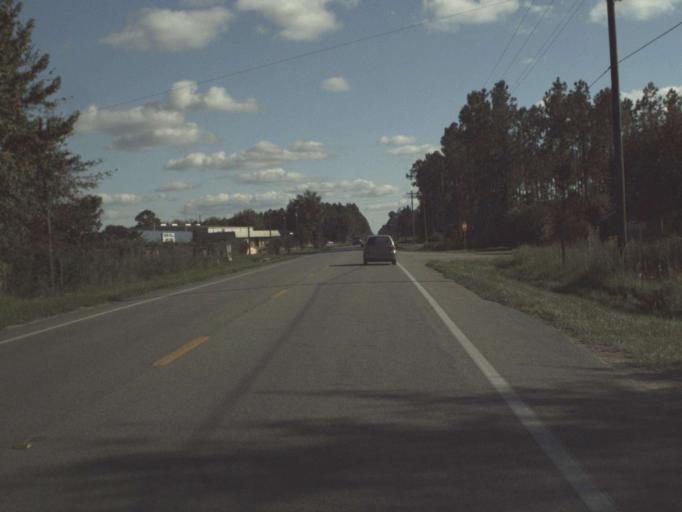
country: US
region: Florida
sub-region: Gulf County
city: Wewahitchka
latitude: 30.0438
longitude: -85.1855
